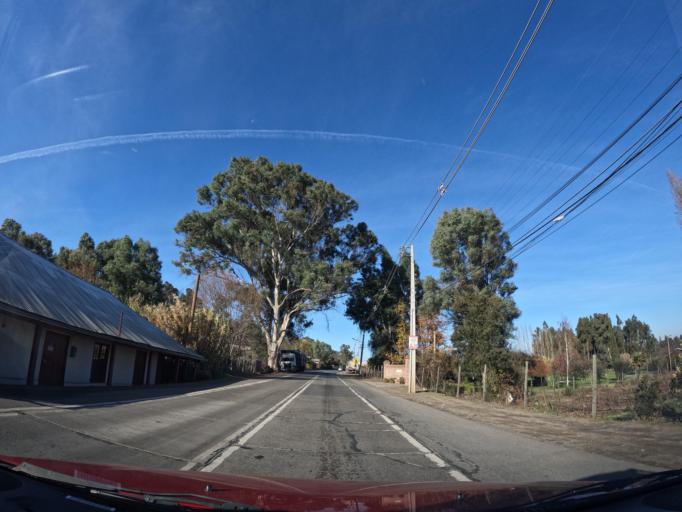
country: CL
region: Maule
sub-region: Provincia de Linares
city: San Javier
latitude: -35.5711
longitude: -71.6951
